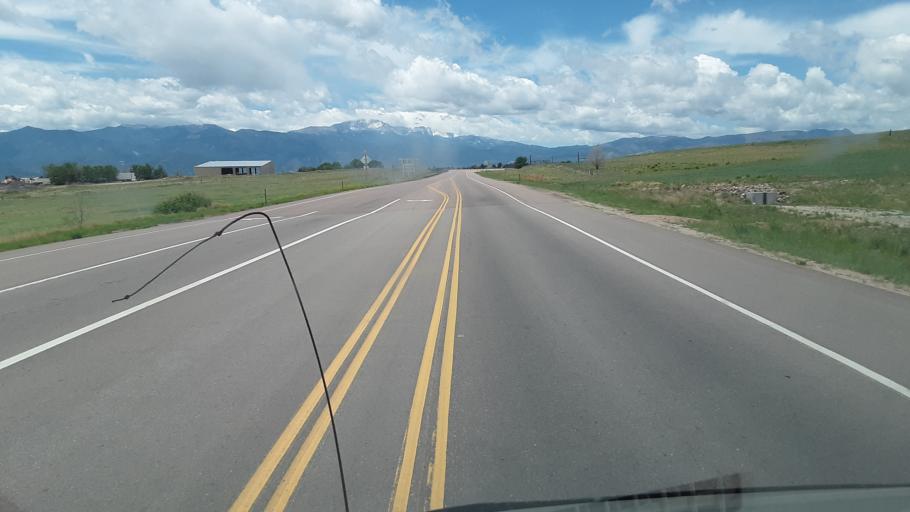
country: US
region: Colorado
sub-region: El Paso County
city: Cimarron Hills
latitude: 38.8416
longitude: -104.6833
